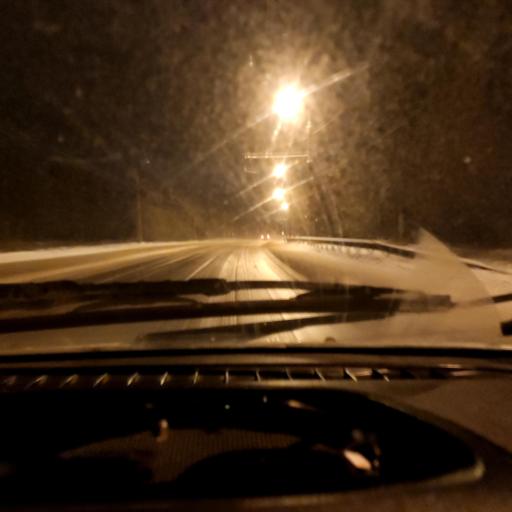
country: RU
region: Samara
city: Zhigulevsk
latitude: 53.4947
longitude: 49.5054
